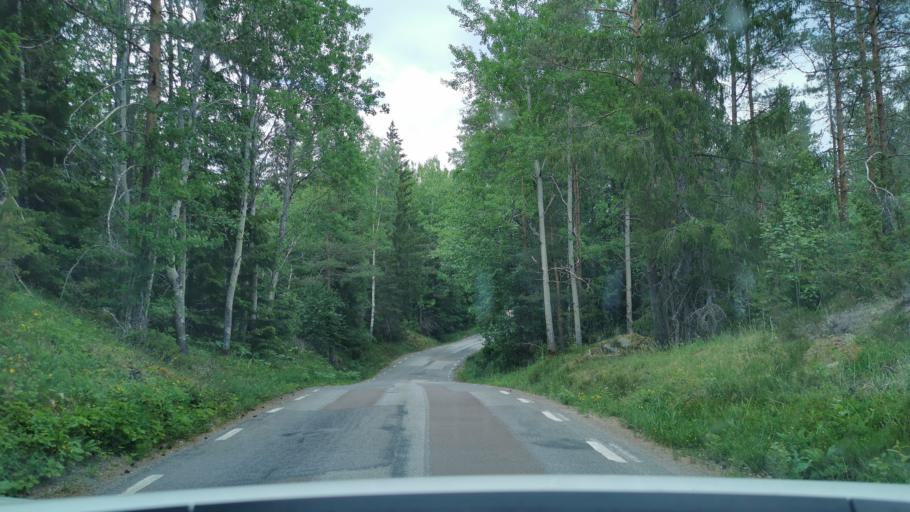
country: SE
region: Vaestra Goetaland
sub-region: Bengtsfors Kommun
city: Dals Langed
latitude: 58.8614
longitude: 12.4022
